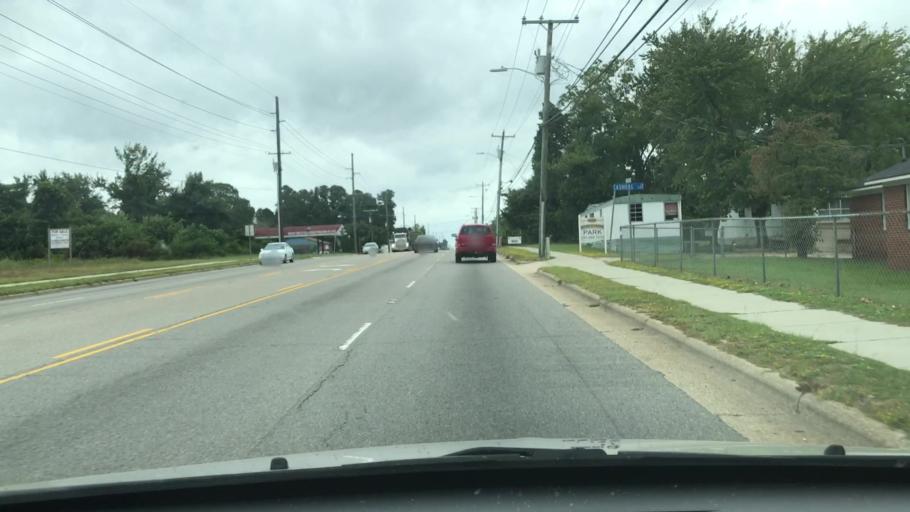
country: US
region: North Carolina
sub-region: Cumberland County
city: Fayetteville
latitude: 35.1050
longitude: -78.9223
